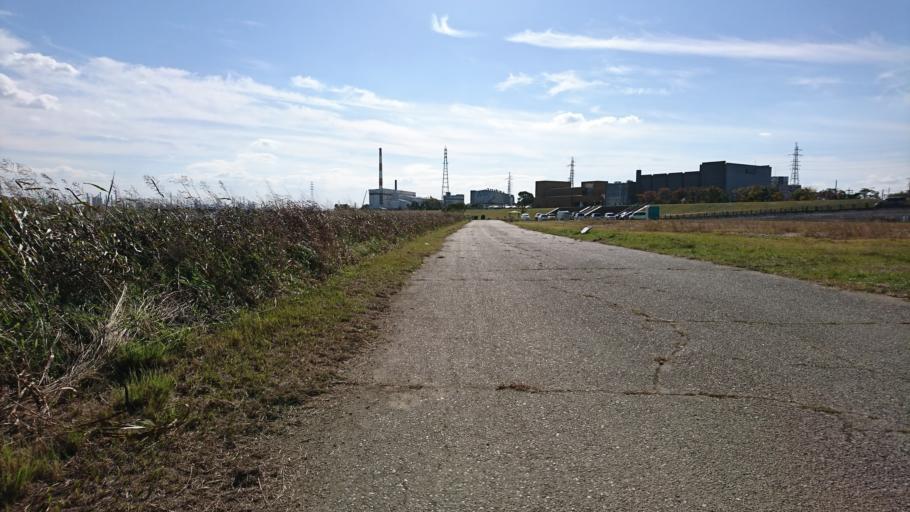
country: JP
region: Hyogo
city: Kakogawacho-honmachi
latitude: 34.7572
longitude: 134.8058
